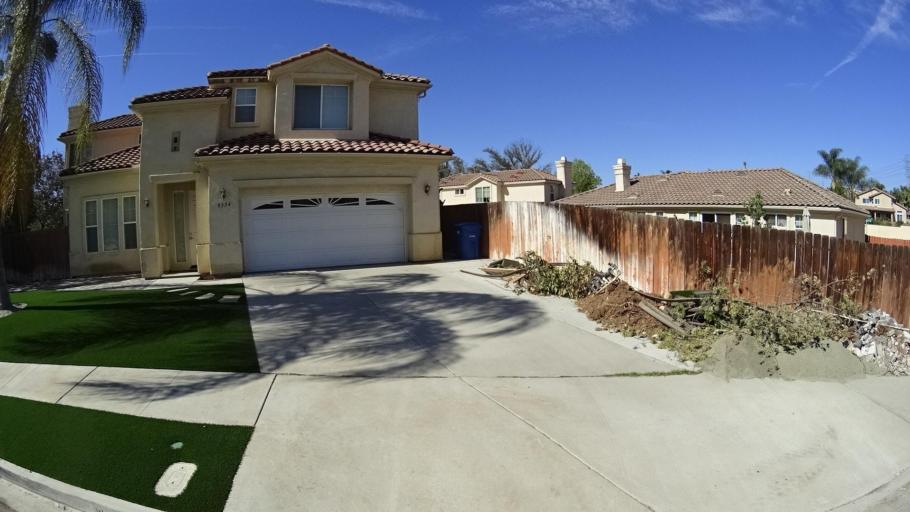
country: US
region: California
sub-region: San Diego County
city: Lakeside
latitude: 32.8453
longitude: -116.8869
